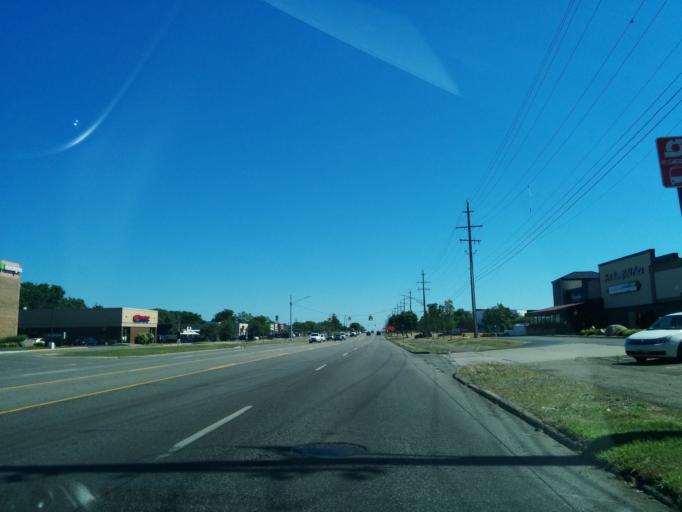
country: US
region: Michigan
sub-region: Oakland County
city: West Bloomfield Township
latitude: 42.5411
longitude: -83.3608
